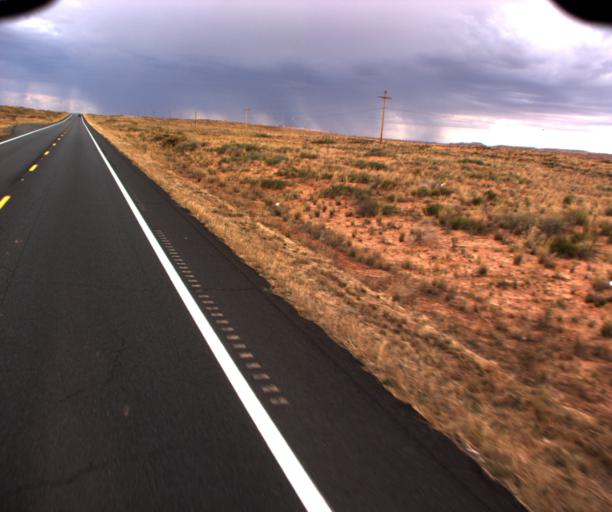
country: US
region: Arizona
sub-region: Coconino County
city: Tuba City
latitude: 36.3006
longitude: -110.9767
